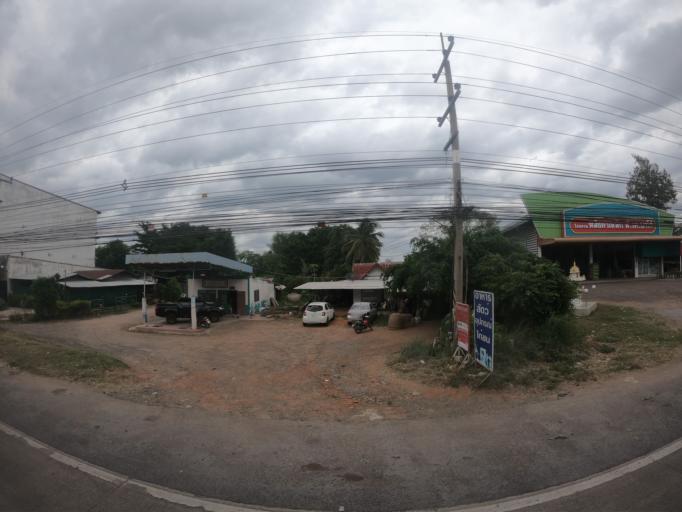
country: TH
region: Nakhon Ratchasima
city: Nakhon Ratchasima
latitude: 14.9073
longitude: 102.1548
